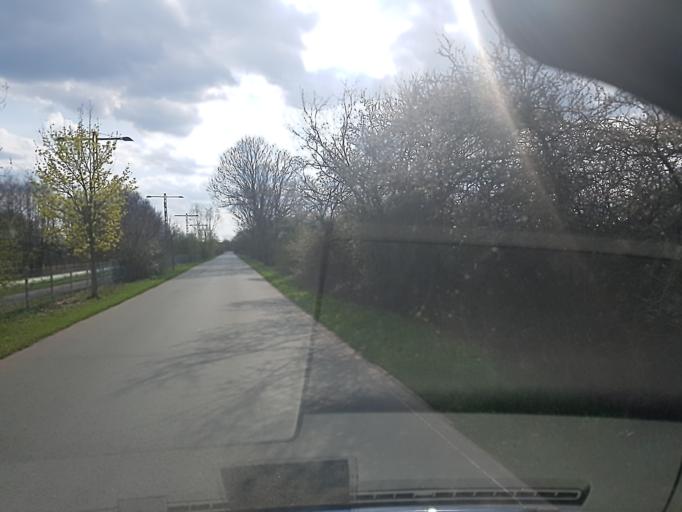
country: DE
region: Saxony-Anhalt
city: Grafenhainichen
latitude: 51.7454
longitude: 12.4319
